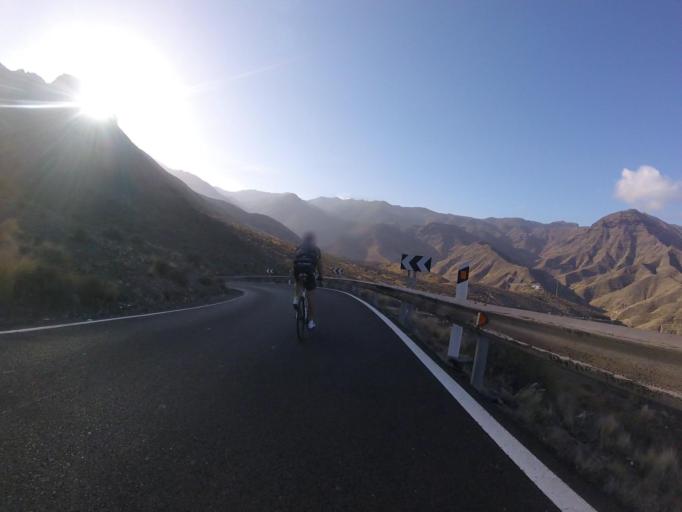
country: ES
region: Canary Islands
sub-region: Provincia de Las Palmas
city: Agaete
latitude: 28.0569
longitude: -15.7315
